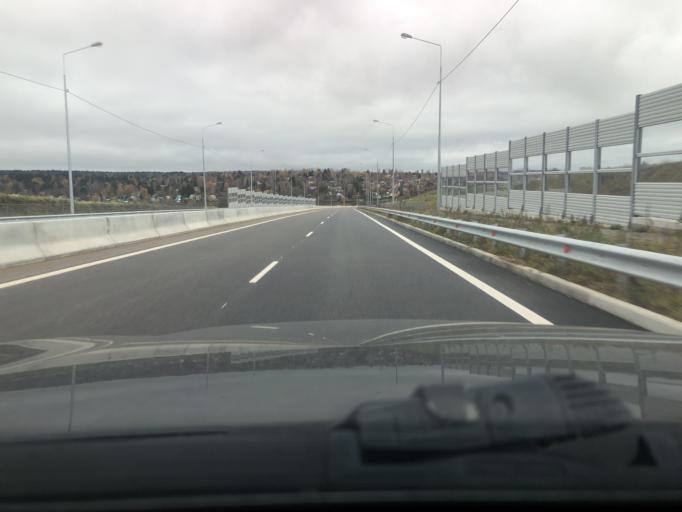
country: RU
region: Moskovskaya
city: Sergiyev Posad
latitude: 56.2964
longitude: 38.1025
